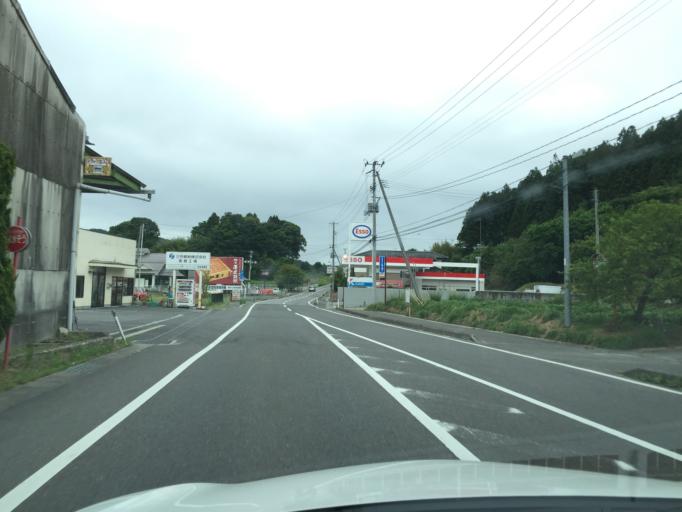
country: JP
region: Fukushima
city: Funehikimachi-funehiki
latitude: 37.3319
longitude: 140.6568
